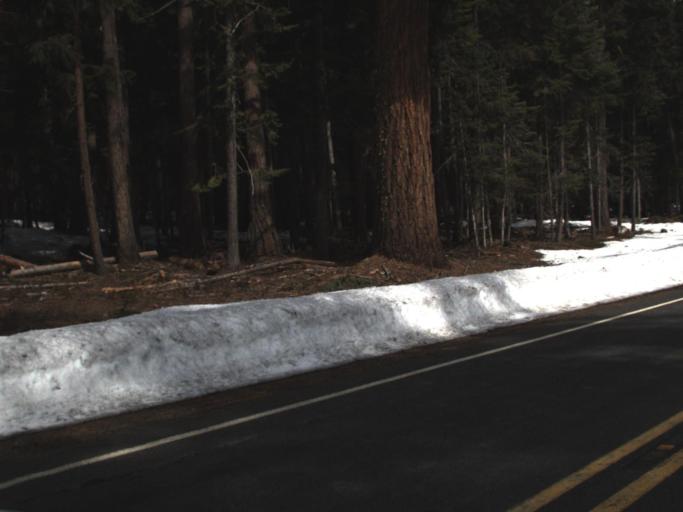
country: US
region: Washington
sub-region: Kittitas County
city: Cle Elum
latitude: 46.9438
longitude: -121.3301
